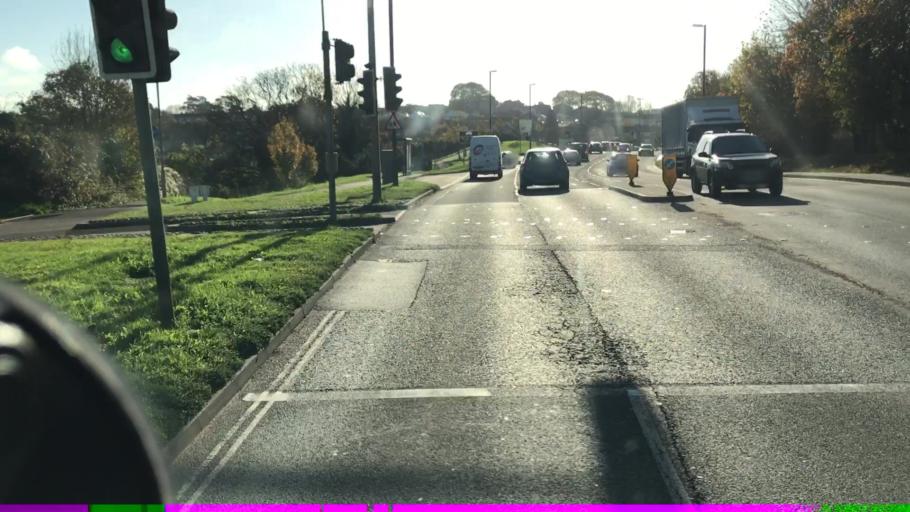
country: GB
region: England
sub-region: Borough of Torbay
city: Paignton
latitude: 50.4264
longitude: -3.5879
